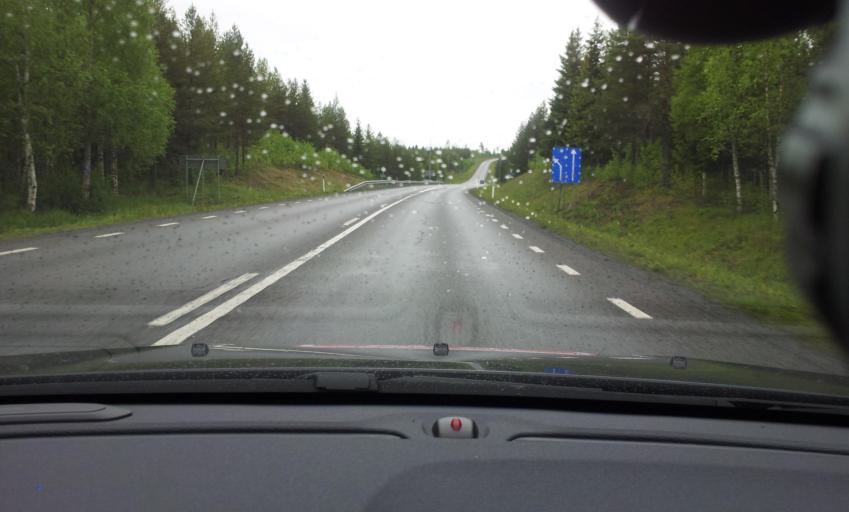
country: SE
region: Jaemtland
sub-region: Krokoms Kommun
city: Valla
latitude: 63.3102
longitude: 13.9233
